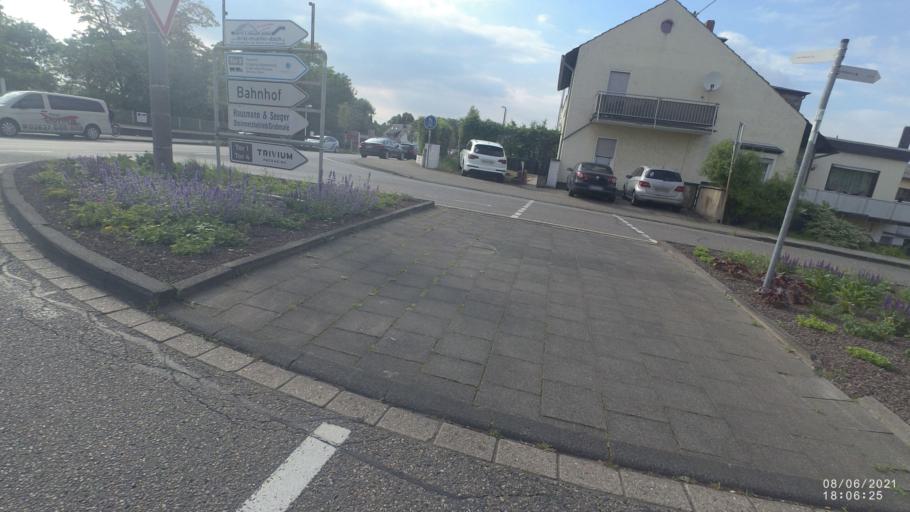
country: DE
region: Rheinland-Pfalz
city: Weissenthurm
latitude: 50.4225
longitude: 7.4457
